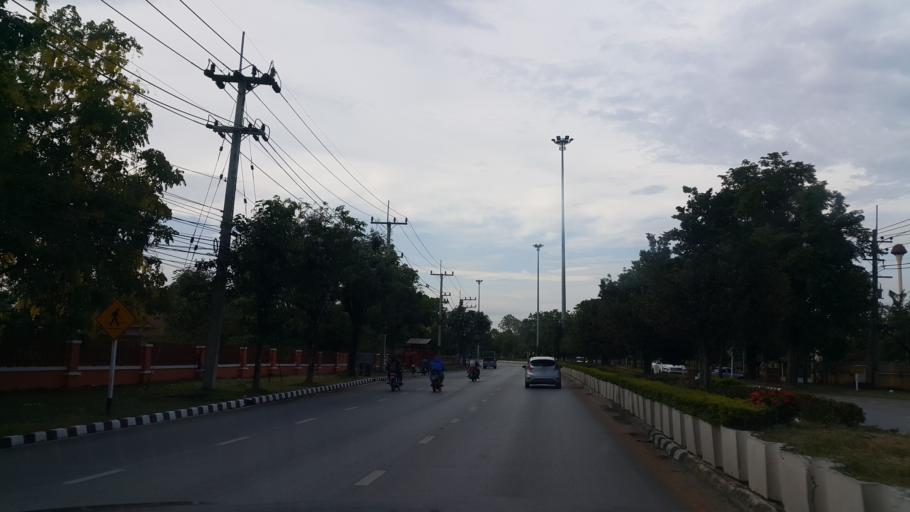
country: TH
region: Chiang Rai
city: Chiang Rai
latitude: 19.9165
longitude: 99.8466
